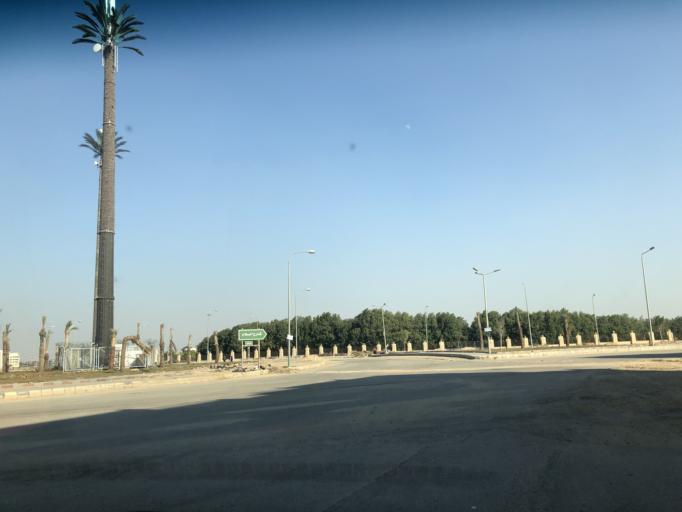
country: EG
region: Al Jizah
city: Madinat Sittah Uktubar
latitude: 29.9344
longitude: 31.0655
